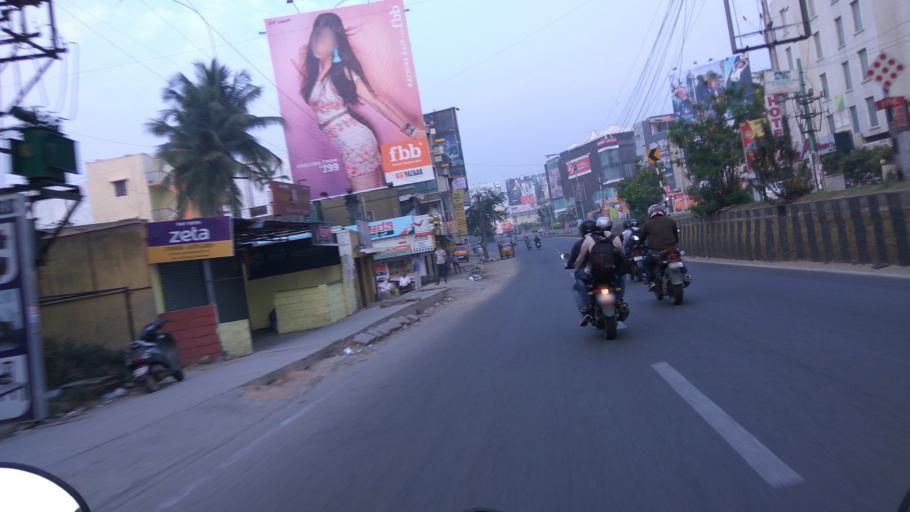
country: IN
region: Karnataka
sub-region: Bangalore Urban
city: Bangalore
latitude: 12.9384
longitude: 77.6305
